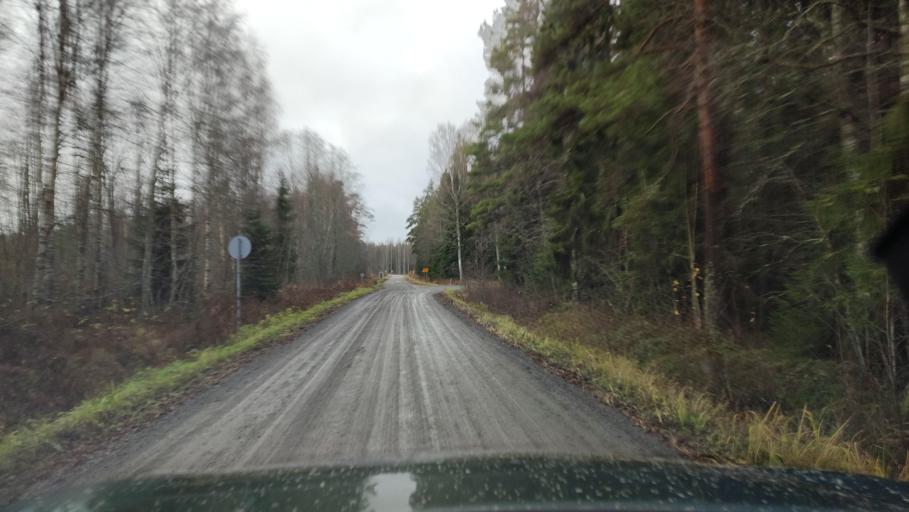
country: FI
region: Ostrobothnia
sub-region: Sydosterbotten
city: Naerpes
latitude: 62.4585
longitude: 21.4942
